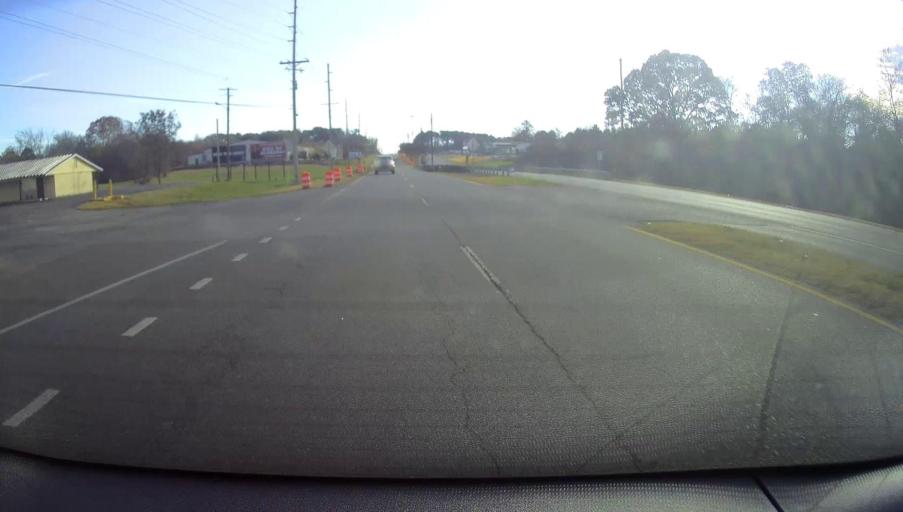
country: US
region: Alabama
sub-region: Limestone County
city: Athens
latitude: 34.7837
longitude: -86.9567
